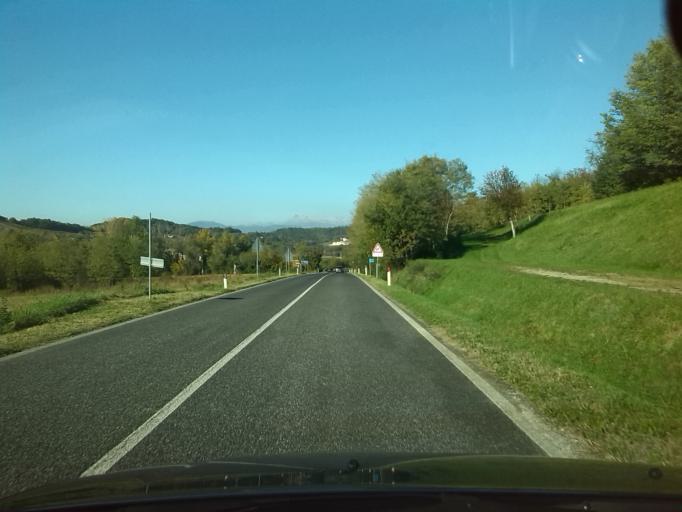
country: IT
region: Friuli Venezia Giulia
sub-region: Provincia di Udine
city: Corno di Rosazzo
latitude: 46.0047
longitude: 13.4667
